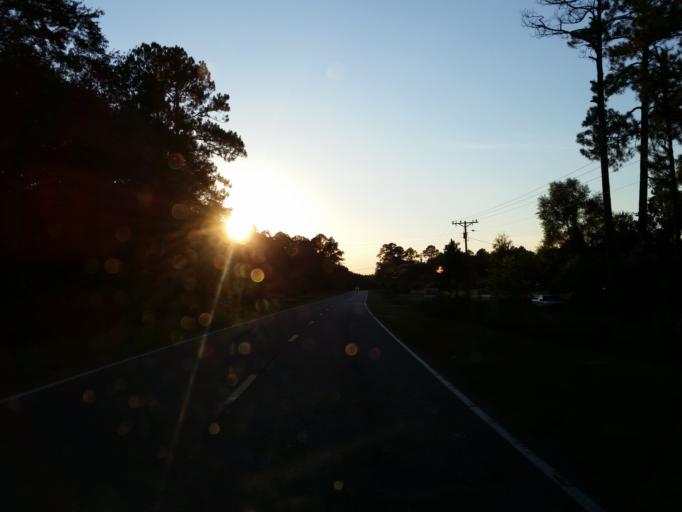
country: US
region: Georgia
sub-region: Berrien County
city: Nashville
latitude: 31.1966
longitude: -83.2204
